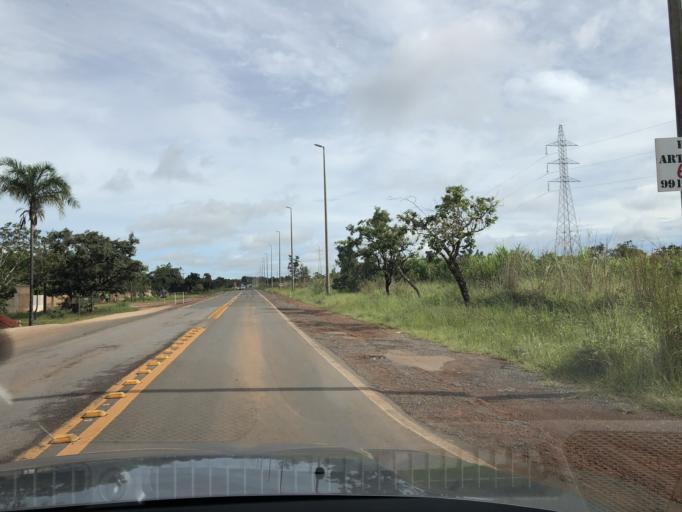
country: BR
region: Federal District
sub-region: Brasilia
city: Brasilia
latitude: -15.6967
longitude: -48.0885
